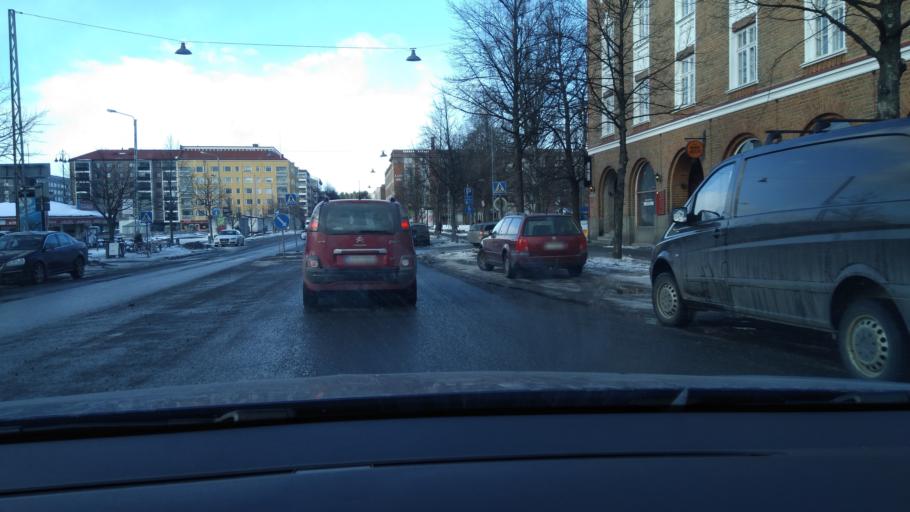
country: FI
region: Pirkanmaa
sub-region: Tampere
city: Tampere
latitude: 61.5006
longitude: 23.7797
